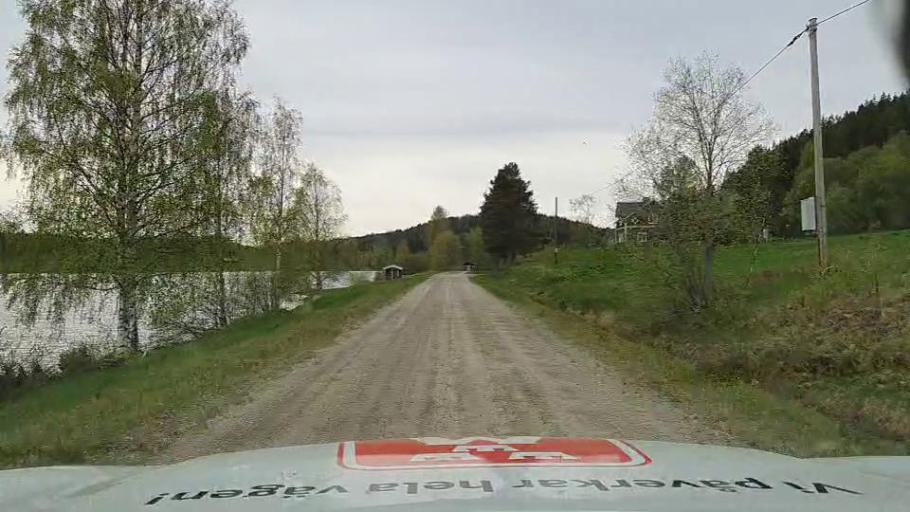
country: SE
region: Jaemtland
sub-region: Bergs Kommun
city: Hoverberg
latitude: 62.6856
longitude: 14.7894
